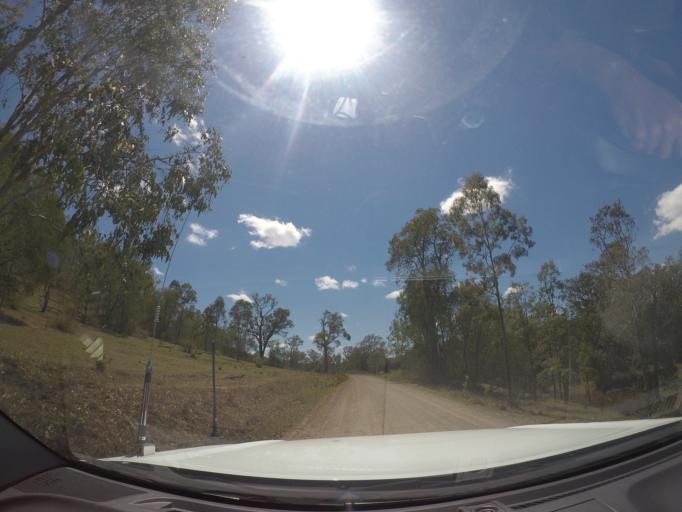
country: AU
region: Queensland
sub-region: Logan
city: Cedar Vale
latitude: -27.8649
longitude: 152.8520
